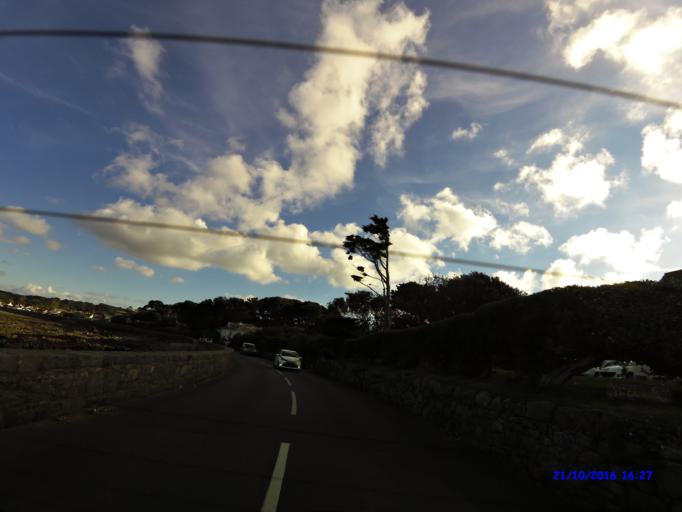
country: GG
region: St Peter Port
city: Saint Peter Port
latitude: 49.4605
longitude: -2.6421
